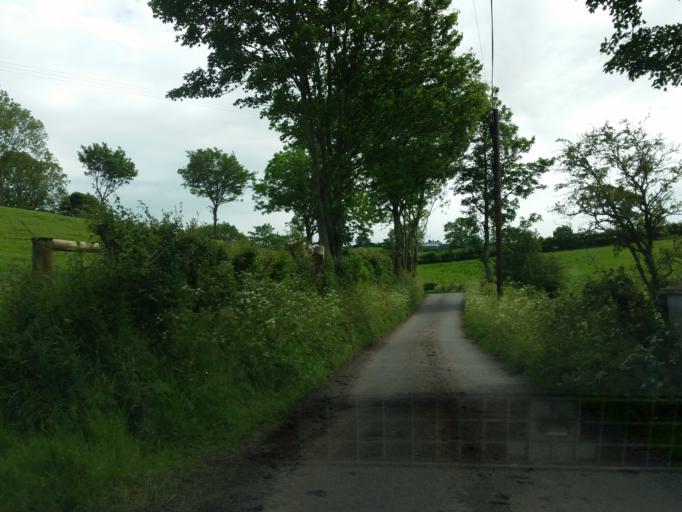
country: GB
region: Northern Ireland
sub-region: Omagh District
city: Omagh
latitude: 54.5422
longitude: -7.1468
